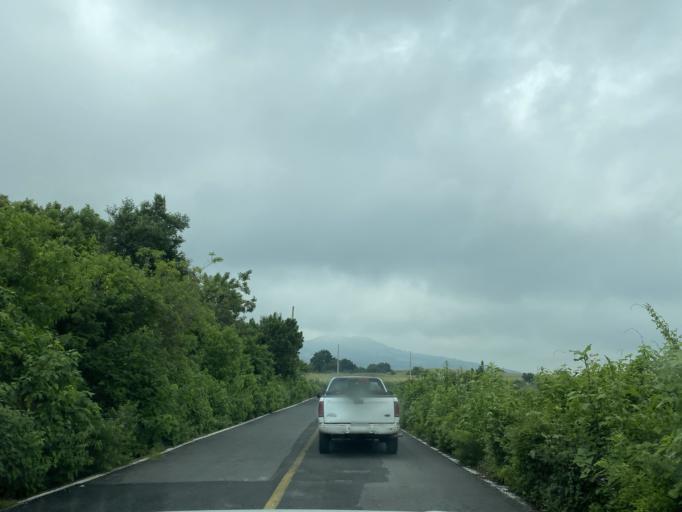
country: MX
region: Morelos
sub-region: Yecapixtla
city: Achichipico
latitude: 18.9623
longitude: -98.8268
